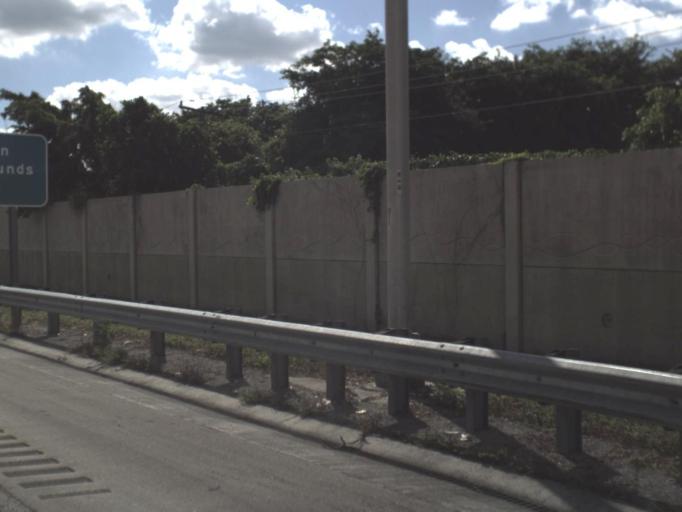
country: US
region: Florida
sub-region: Broward County
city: Broadview Park
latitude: 26.1122
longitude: -80.2187
